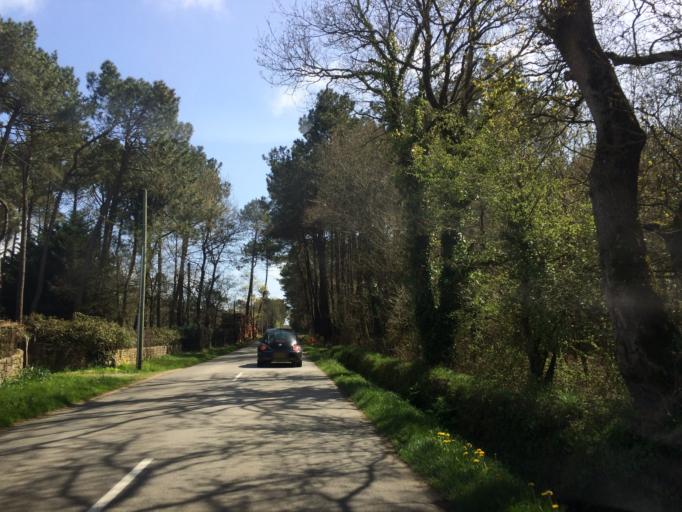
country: FR
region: Brittany
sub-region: Departement du Morbihan
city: La Trinite-sur-Mer
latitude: 47.6135
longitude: -3.0519
